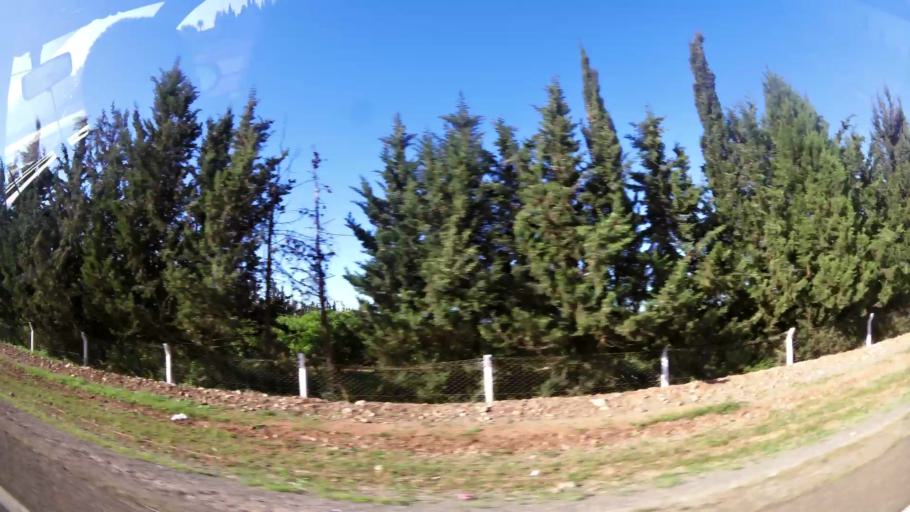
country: MA
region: Oriental
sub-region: Berkane-Taourirt
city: Ahfir
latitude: 35.0018
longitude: -2.1778
